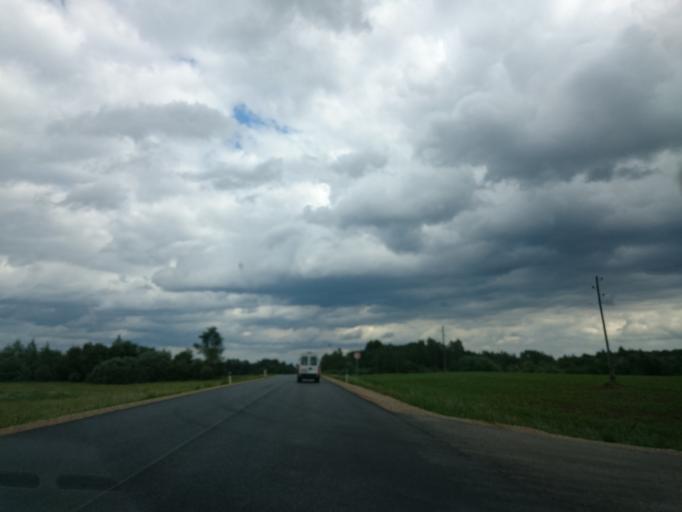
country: LV
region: Ludzas Rajons
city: Ludza
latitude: 56.5255
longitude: 27.5273
